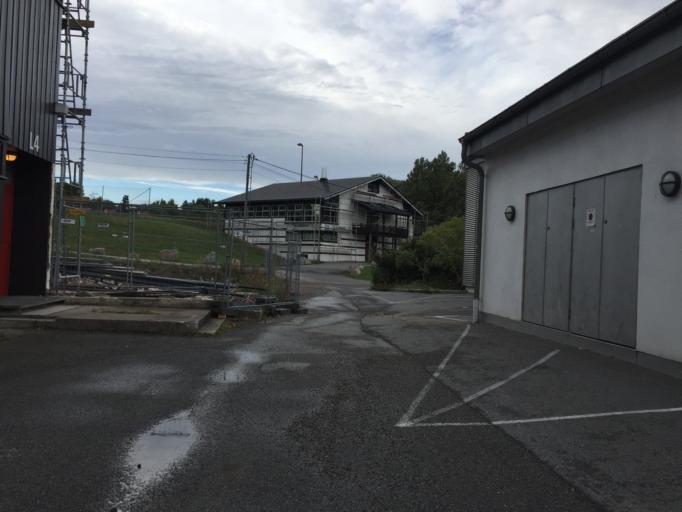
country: NO
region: Oslo
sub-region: Oslo
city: Oslo
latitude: 59.8956
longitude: 10.8259
